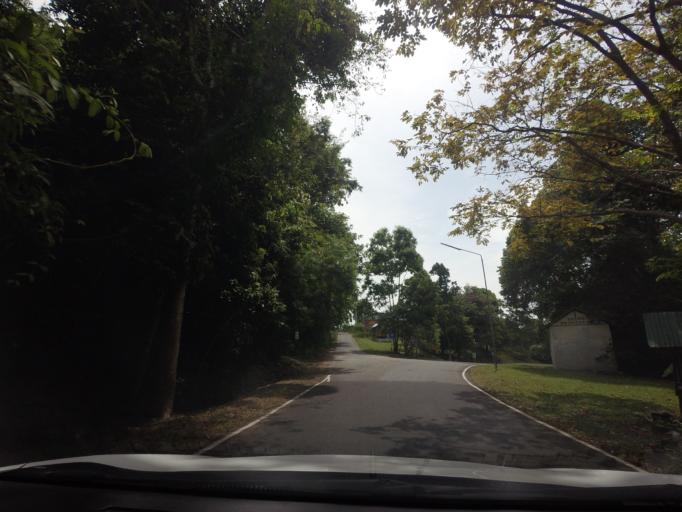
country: TH
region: Chon Buri
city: Ban Bueng
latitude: 13.2092
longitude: 101.0554
